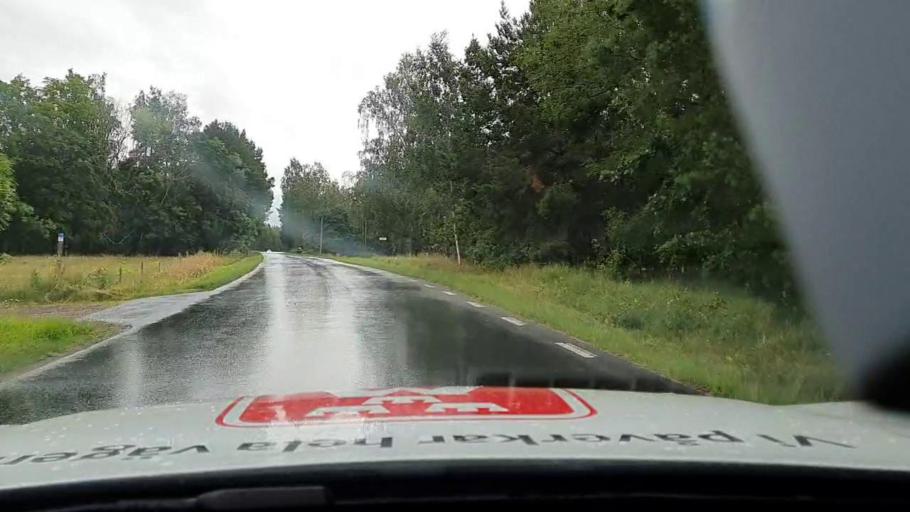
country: SE
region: Vaestra Goetaland
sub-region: Skovde Kommun
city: Stopen
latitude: 58.5396
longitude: 13.9568
